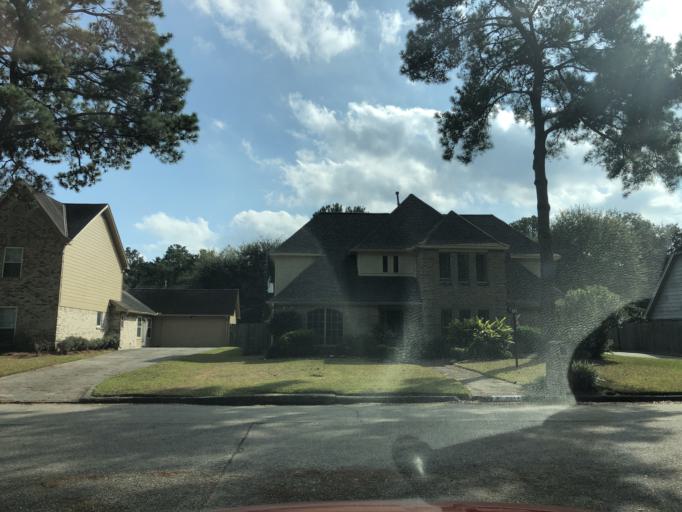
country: US
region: Texas
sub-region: Harris County
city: Tomball
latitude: 30.0211
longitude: -95.5446
